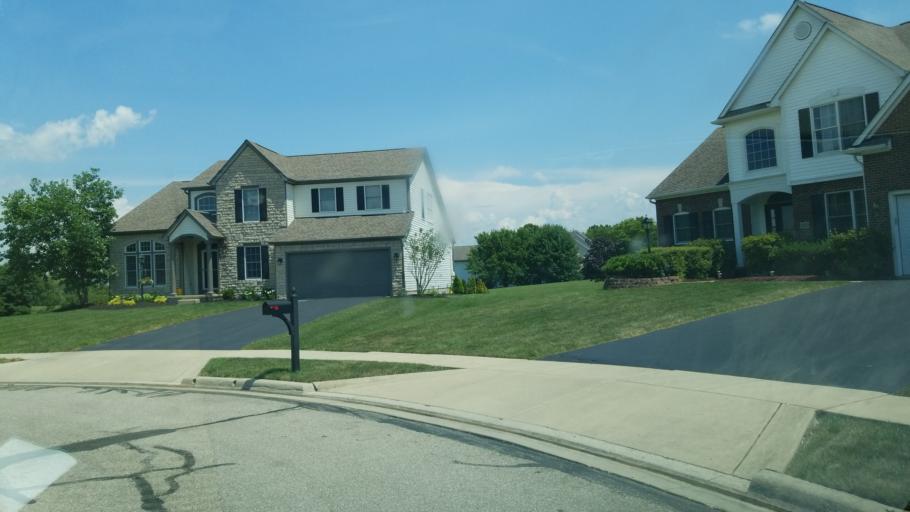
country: US
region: Ohio
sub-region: Delaware County
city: Lewis Center
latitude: 40.2185
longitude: -82.9925
